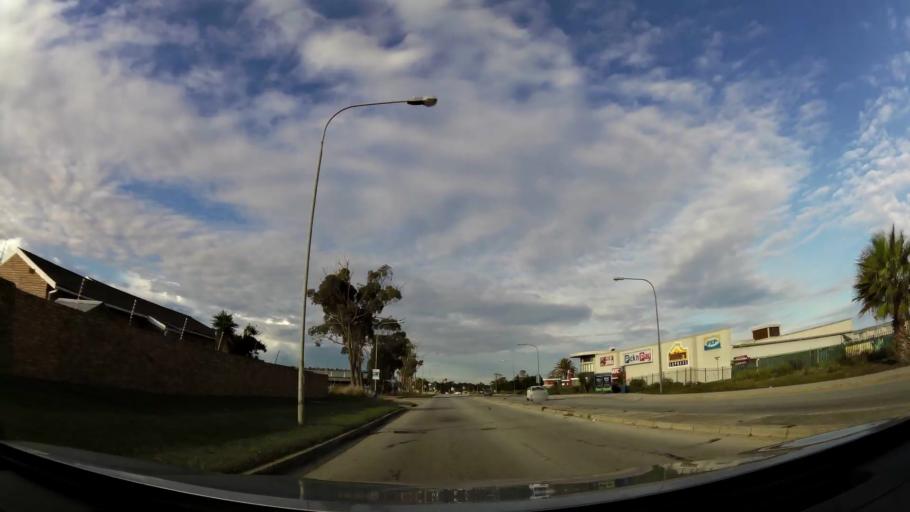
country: ZA
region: Eastern Cape
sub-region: Nelson Mandela Bay Metropolitan Municipality
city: Port Elizabeth
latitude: -33.9574
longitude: 25.5011
